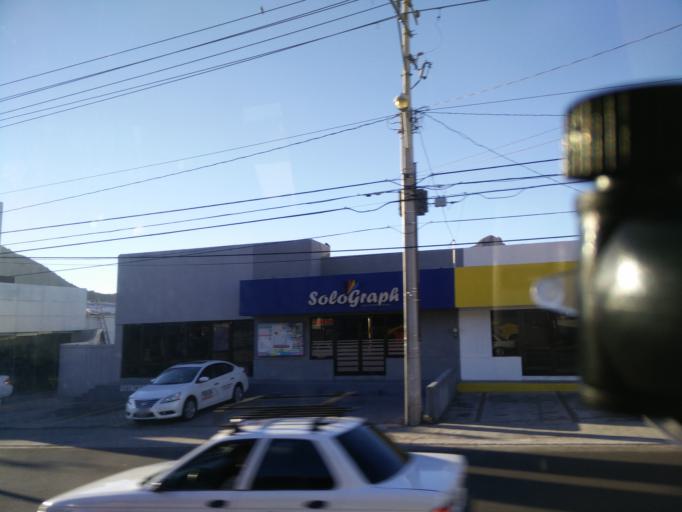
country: MX
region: Sonora
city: Heroica Guaymas
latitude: 27.9255
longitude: -110.9165
